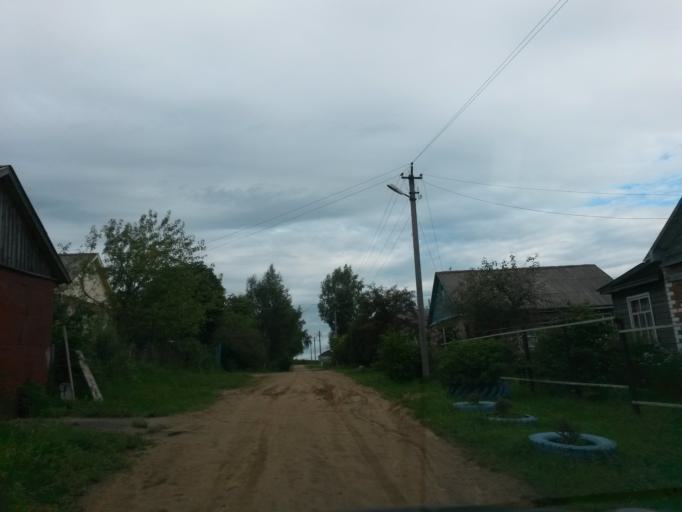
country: RU
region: Jaroslavl
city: Gavrilov-Yam
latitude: 57.3082
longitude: 39.9518
